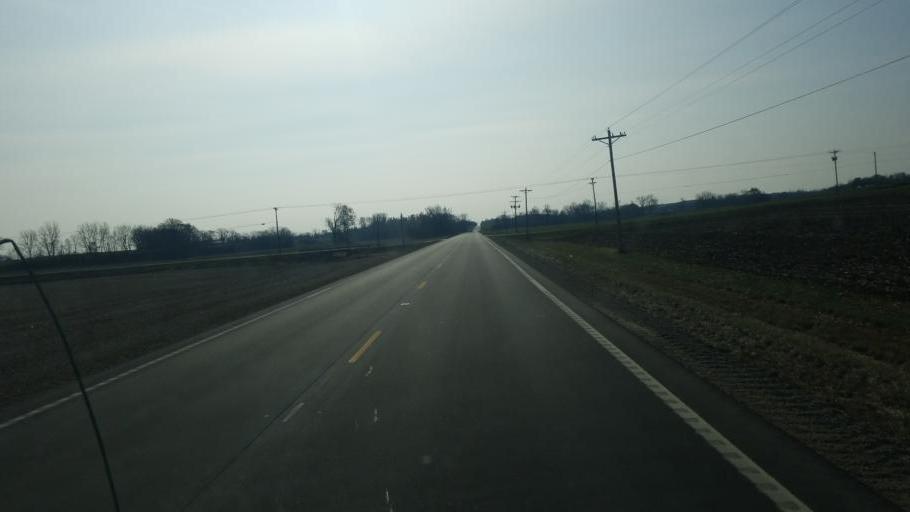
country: US
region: Ohio
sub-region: Mercer County
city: Fort Recovery
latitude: 40.4666
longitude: -84.7844
